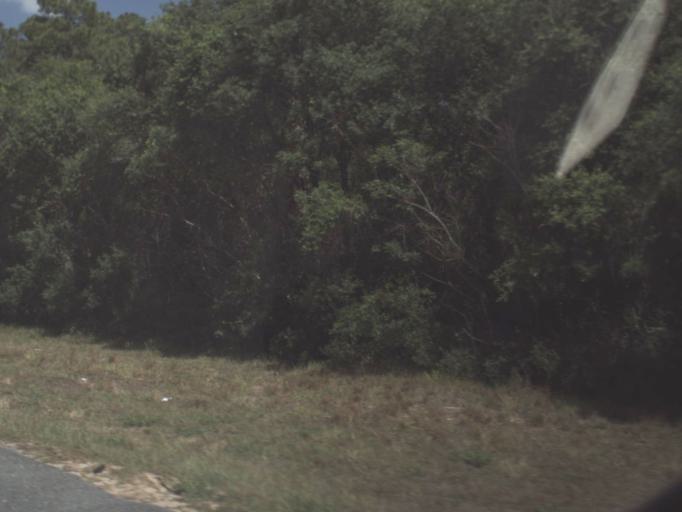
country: US
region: Florida
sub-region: Lake County
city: Astor
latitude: 29.1769
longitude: -81.7023
